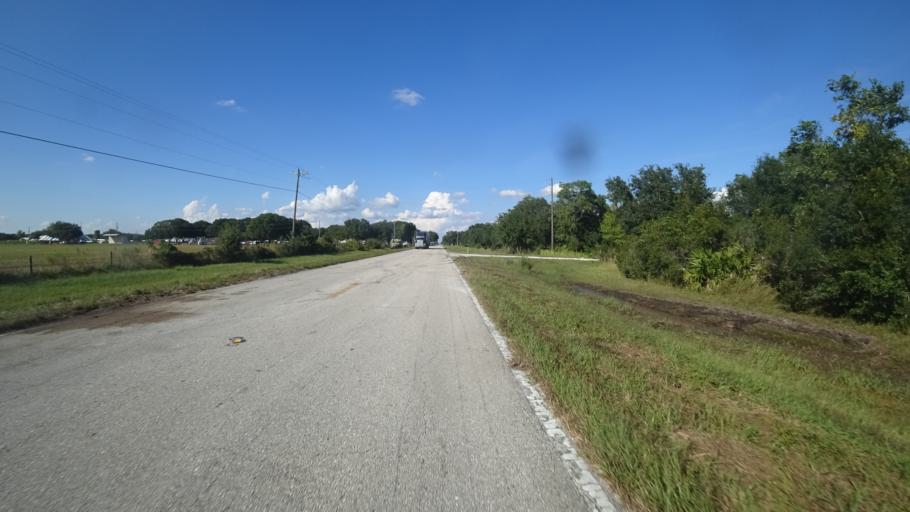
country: US
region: Florida
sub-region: Sarasota County
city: The Meadows
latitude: 27.4422
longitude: -82.3034
